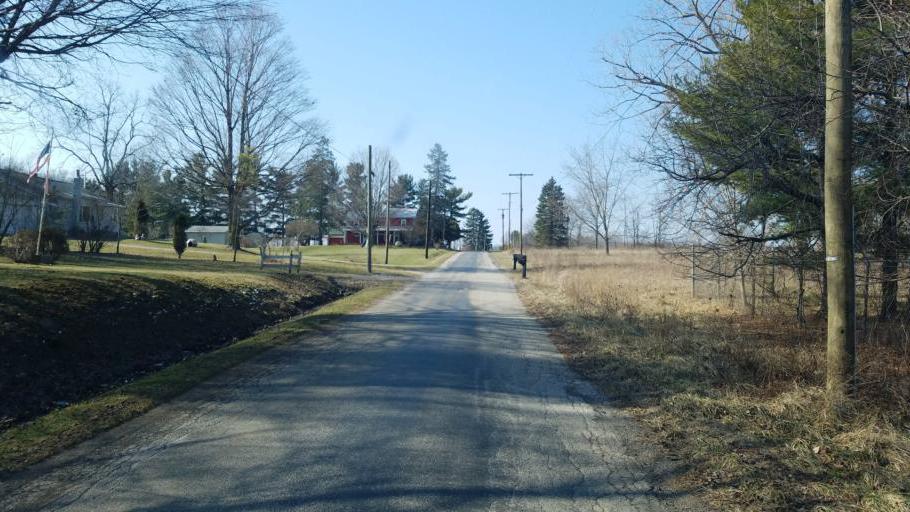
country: US
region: Ohio
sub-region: Richland County
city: Mansfield
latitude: 40.8287
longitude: -82.5287
